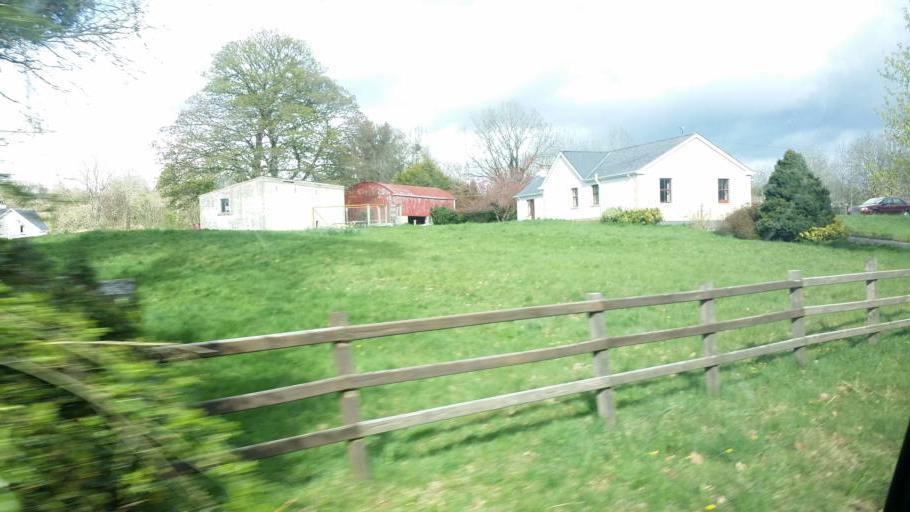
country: IE
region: Connaught
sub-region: County Leitrim
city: Manorhamilton
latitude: 54.3188
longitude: -8.1985
